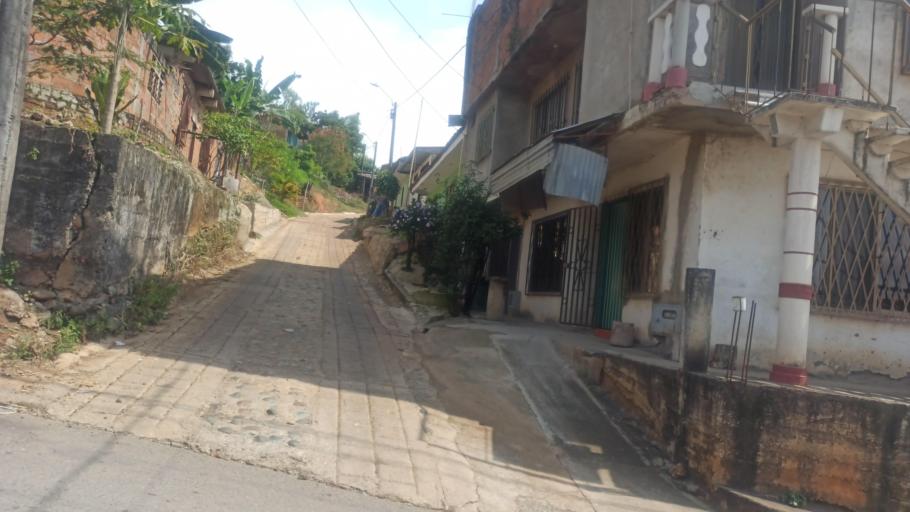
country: CO
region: Cauca
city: Buenos Aires
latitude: 3.1287
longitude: -76.5954
